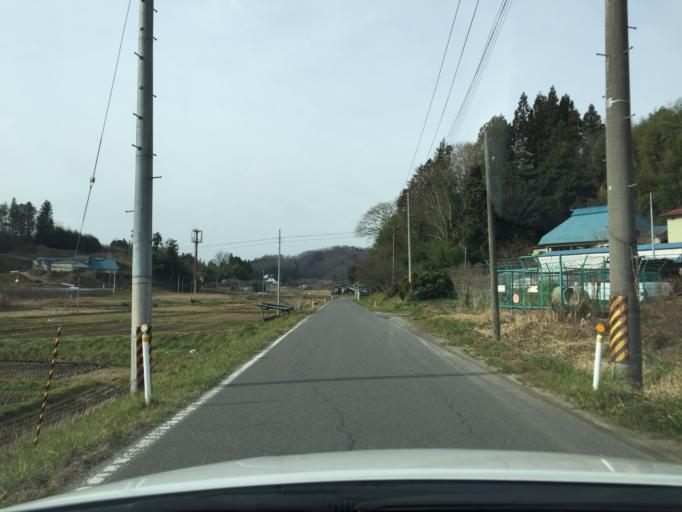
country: JP
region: Fukushima
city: Funehikimachi-funehiki
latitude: 37.4133
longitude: 140.5817
